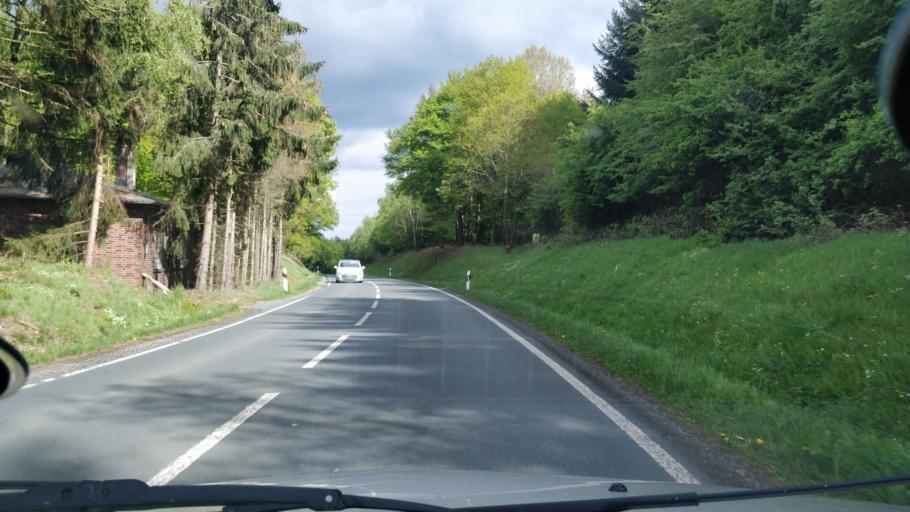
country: DE
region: Hesse
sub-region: Regierungsbezirk Darmstadt
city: Neu-Anspach
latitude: 50.3338
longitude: 8.4882
